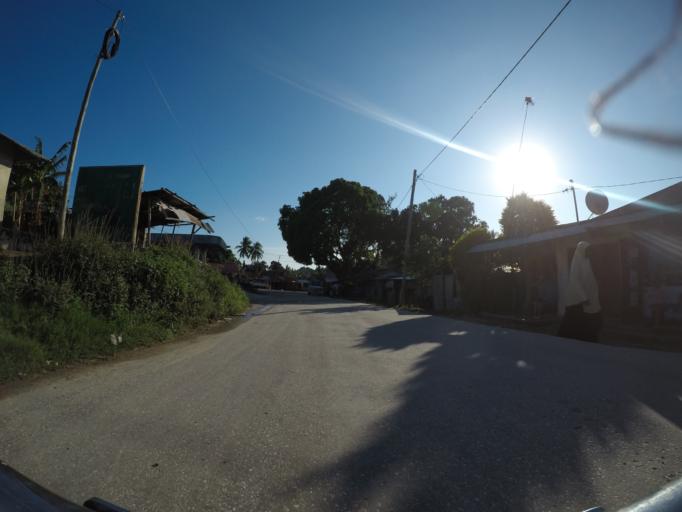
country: TZ
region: Pemba South
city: Mtambile
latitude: -5.3780
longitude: 39.7011
